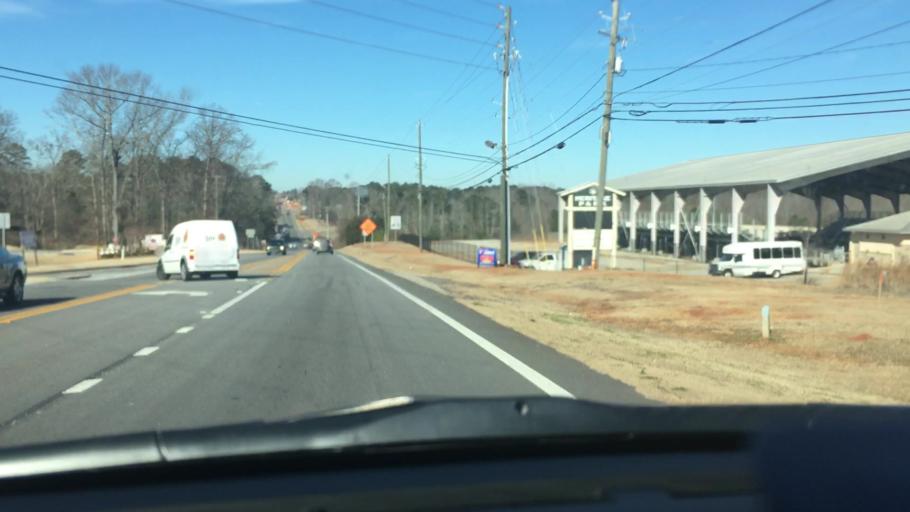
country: US
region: Georgia
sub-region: Henry County
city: McDonough
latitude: 33.4399
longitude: -84.1228
